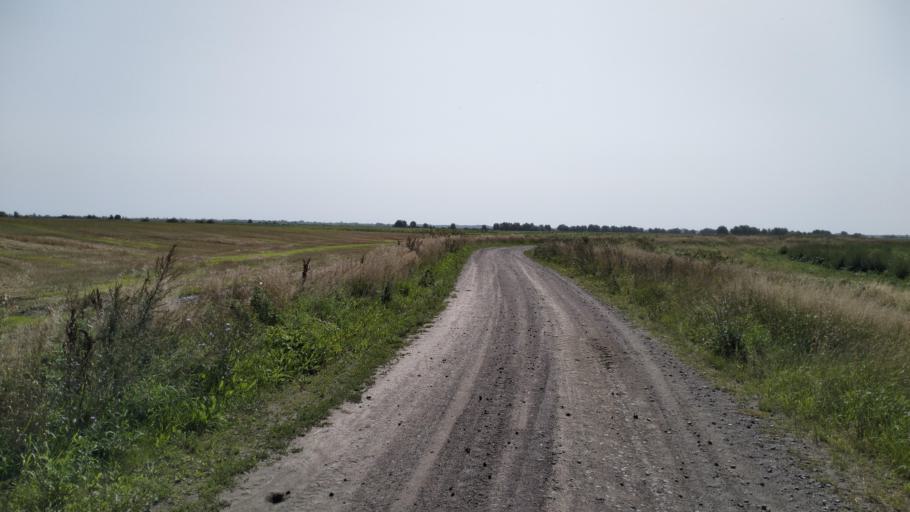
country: BY
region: Brest
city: Davyd-Haradok
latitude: 52.0083
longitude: 27.1662
